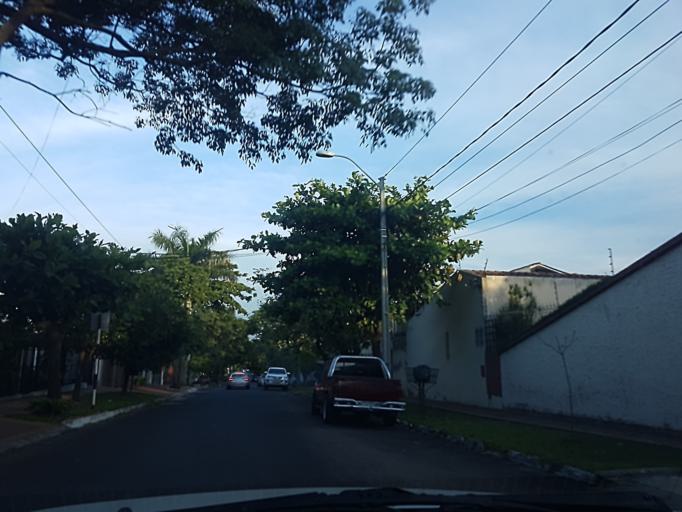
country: PY
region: Asuncion
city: Asuncion
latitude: -25.2856
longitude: -57.5960
